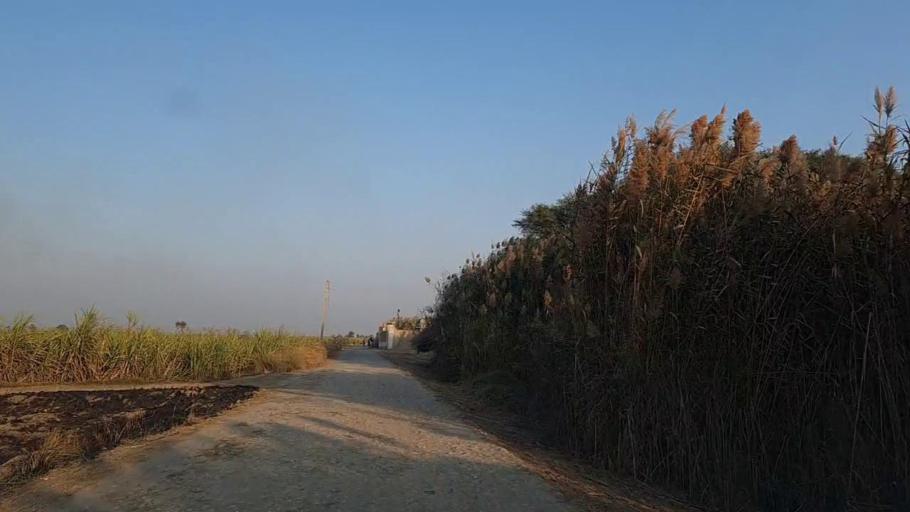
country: PK
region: Sindh
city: Daur
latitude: 26.5107
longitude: 68.2962
